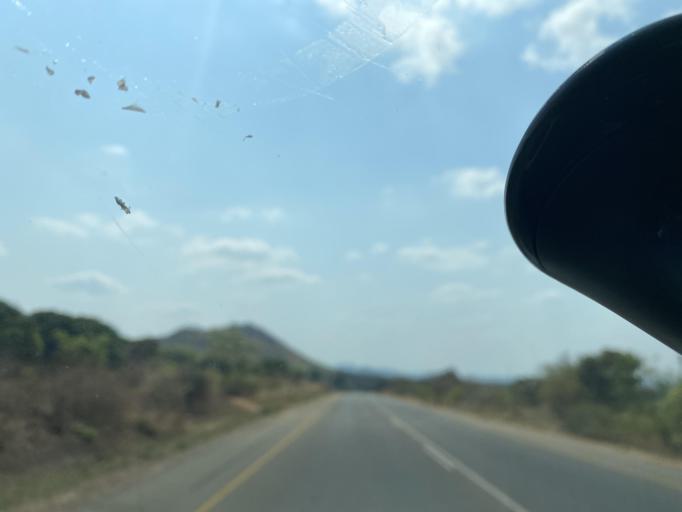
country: ZM
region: Lusaka
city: Chongwe
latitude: -15.5979
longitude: 28.7245
